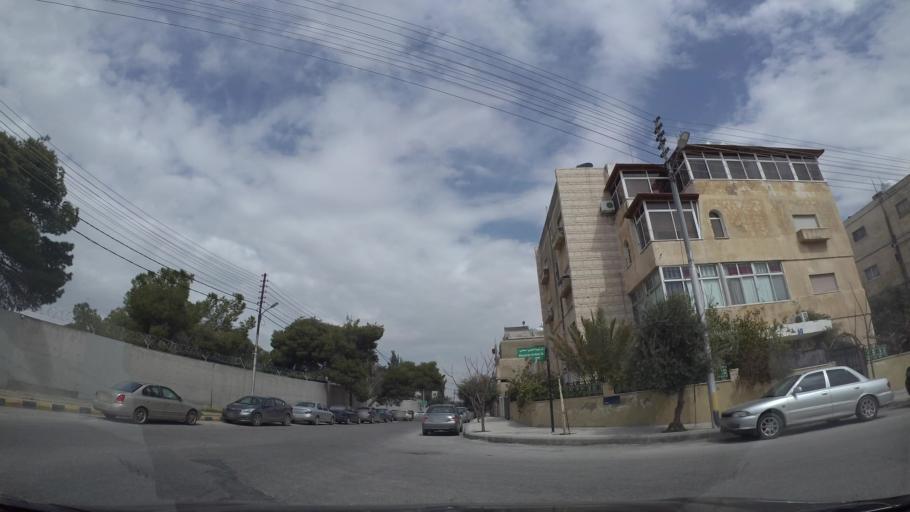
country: JO
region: Amman
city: Amman
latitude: 31.9628
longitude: 35.9488
